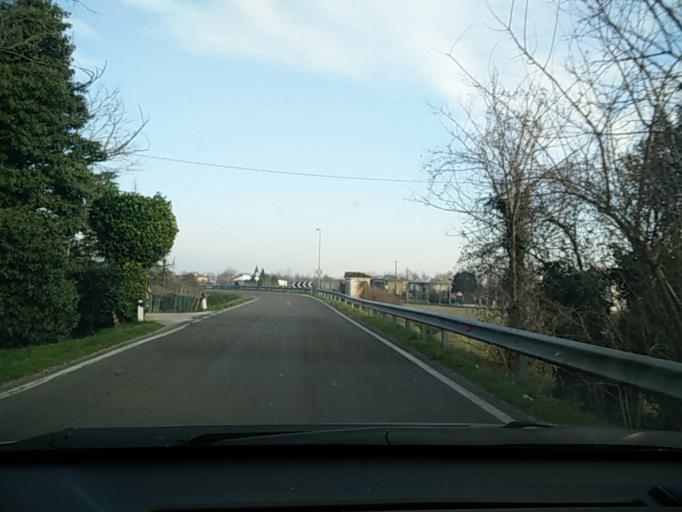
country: IT
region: Veneto
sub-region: Provincia di Venezia
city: Fossalta di Piave
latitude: 45.6547
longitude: 12.5113
